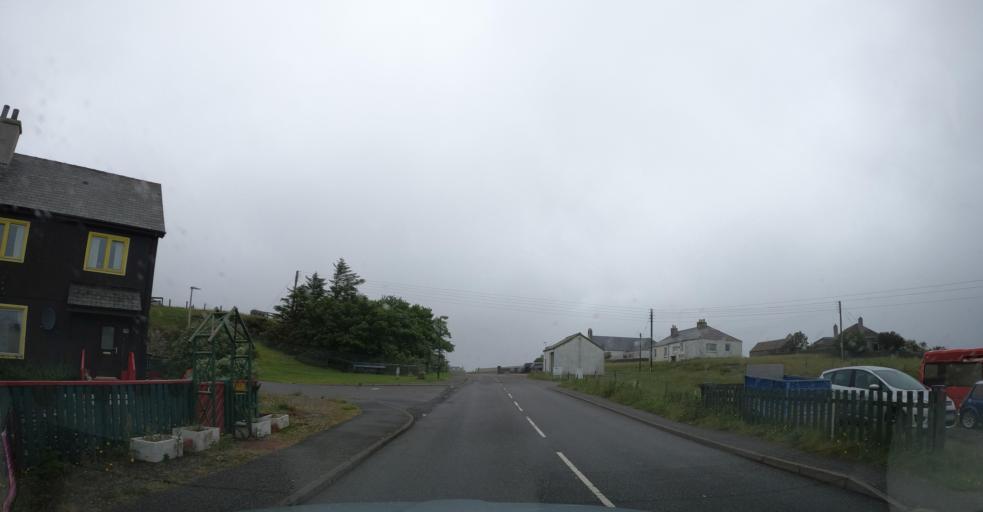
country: GB
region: Scotland
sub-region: Eilean Siar
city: Isle of North Uist
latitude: 57.5999
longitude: -7.1609
